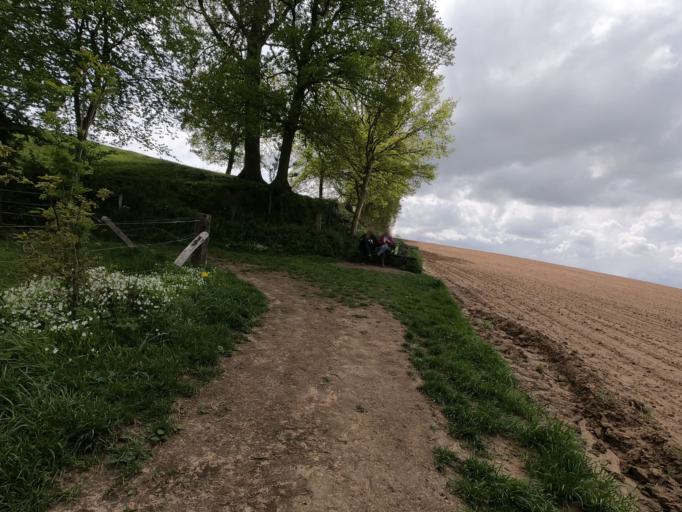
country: BE
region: Flanders
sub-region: Provincie Oost-Vlaanderen
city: Ronse
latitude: 50.7646
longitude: 3.5661
